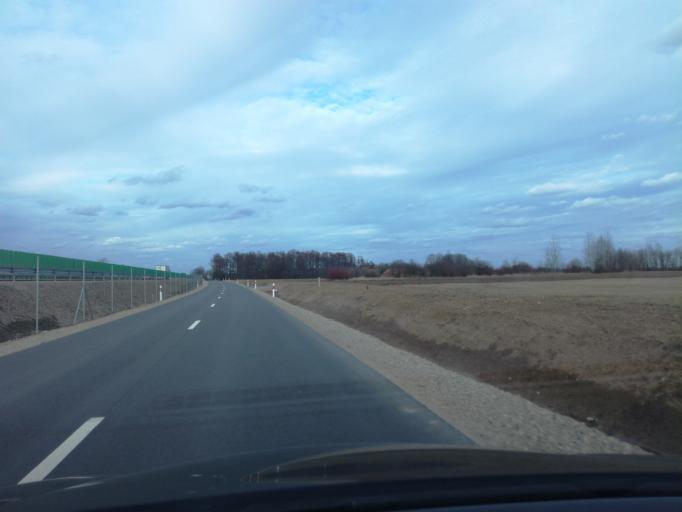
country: LT
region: Marijampoles apskritis
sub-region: Marijampole Municipality
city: Marijampole
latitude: 54.6014
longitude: 23.4031
